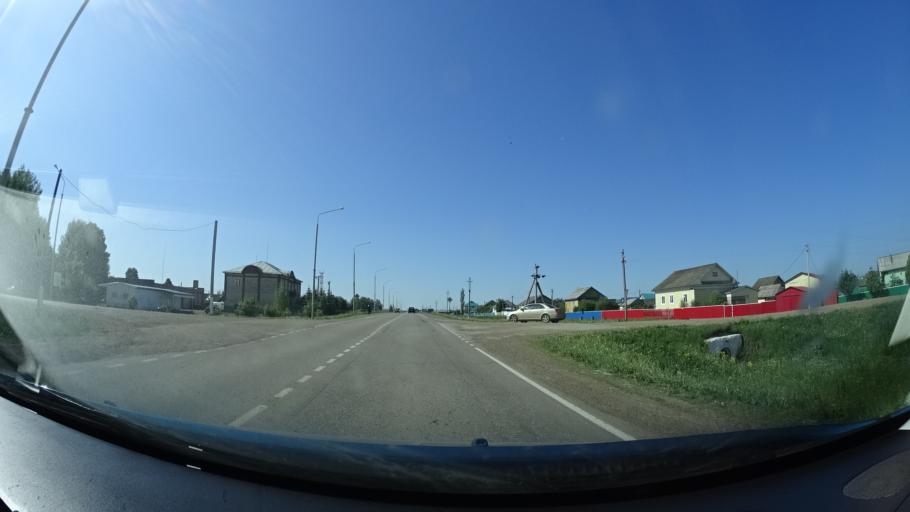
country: RU
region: Bashkortostan
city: Starobaltachevo
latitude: 56.0120
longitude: 55.9054
